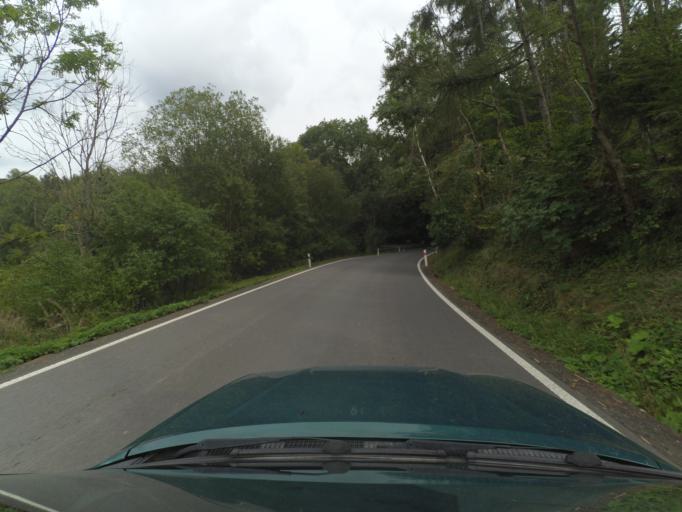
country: CZ
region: Central Bohemia
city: Revnicov
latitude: 50.2088
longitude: 13.7534
